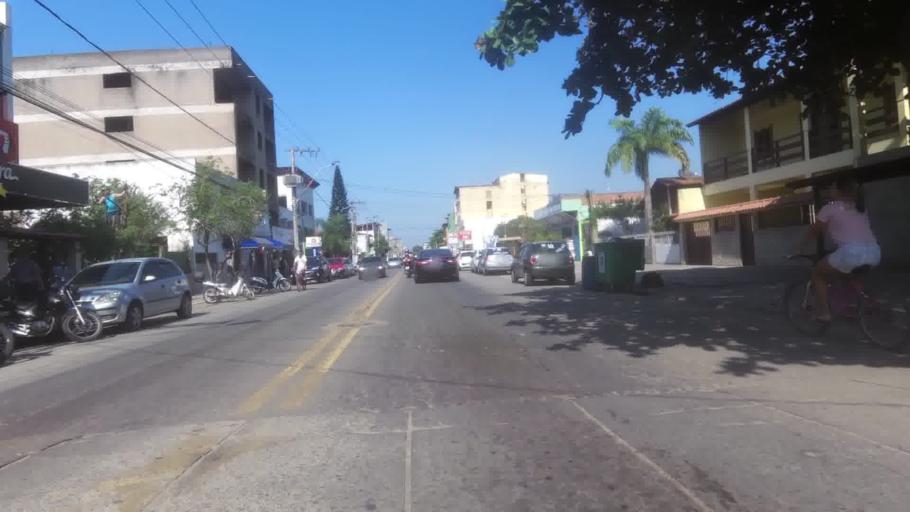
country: BR
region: Espirito Santo
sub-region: Marataizes
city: Marataizes
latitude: -21.0355
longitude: -40.8189
